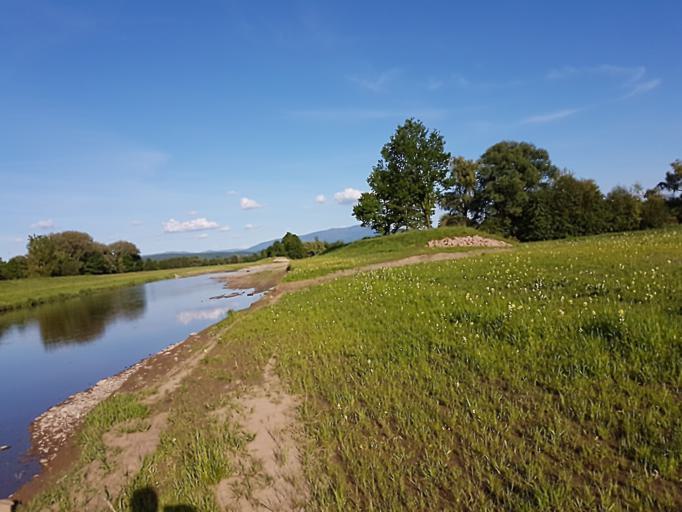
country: DE
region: Baden-Wuerttemberg
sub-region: Freiburg Region
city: Teningen
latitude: 48.1394
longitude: 7.7850
